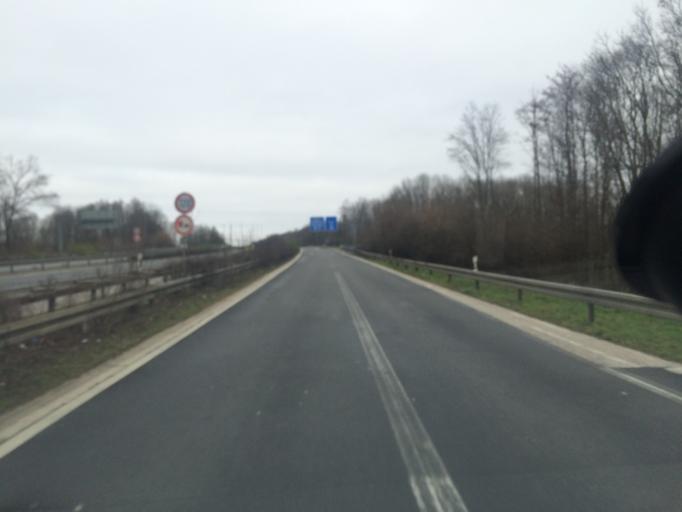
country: DE
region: North Rhine-Westphalia
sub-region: Regierungsbezirk Arnsberg
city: Bochum
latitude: 51.4958
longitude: 7.2726
